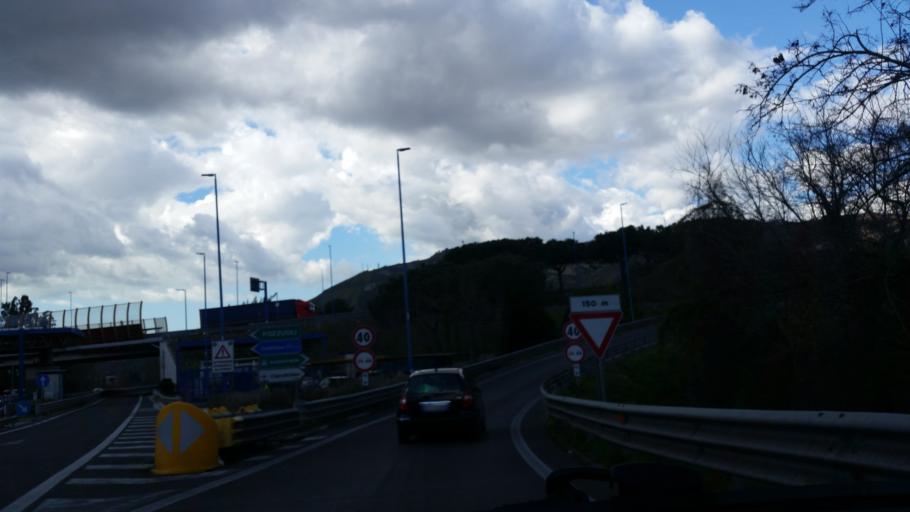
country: IT
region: Campania
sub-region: Provincia di Napoli
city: Napoli
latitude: 40.8435
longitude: 14.2169
